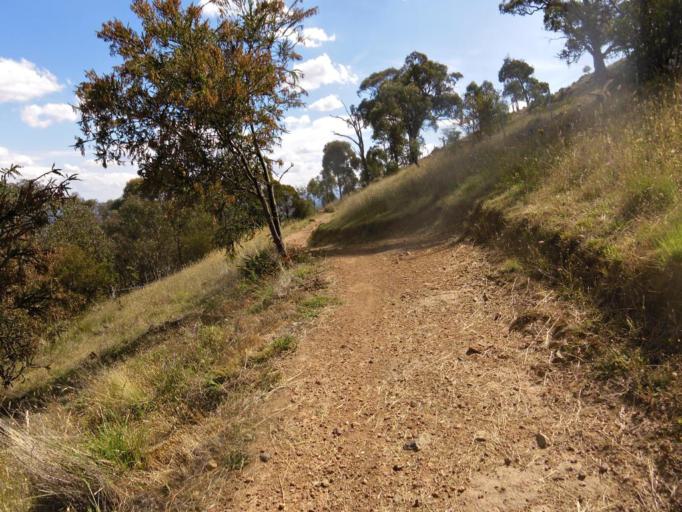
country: AU
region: Australian Capital Territory
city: Belconnen
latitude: -35.1561
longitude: 149.0817
